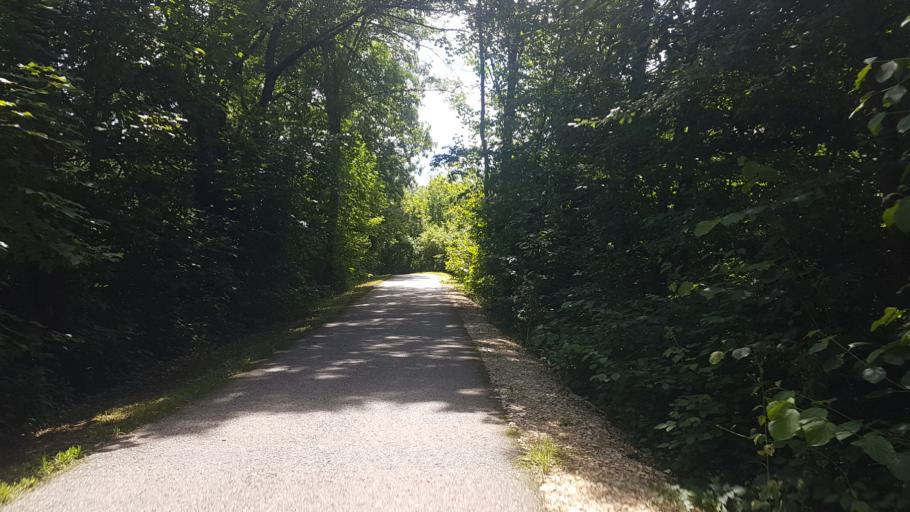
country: DE
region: Bavaria
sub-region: Upper Bavaria
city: Eichstaett
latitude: 48.8897
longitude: 11.1672
